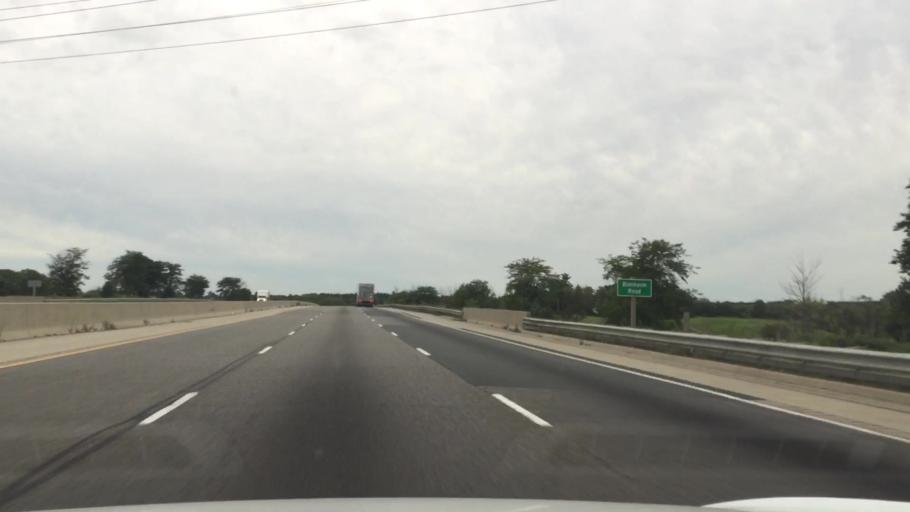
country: CA
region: Ontario
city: Kitchener
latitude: 43.2790
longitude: -80.5223
